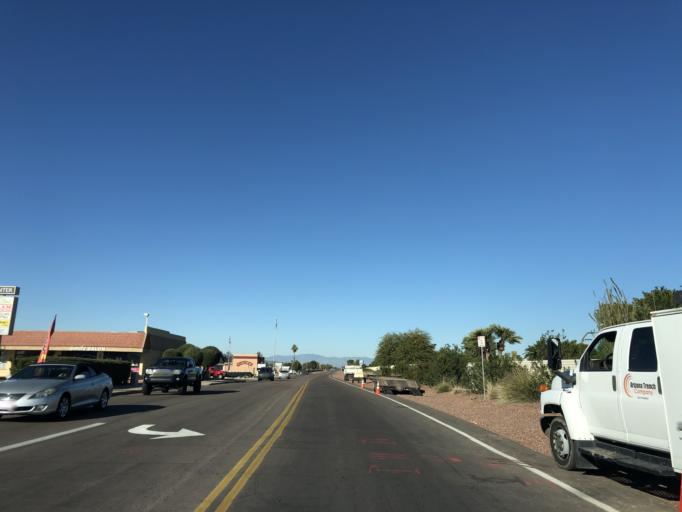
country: US
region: Arizona
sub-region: Maricopa County
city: Surprise
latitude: 33.6529
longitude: -112.2899
